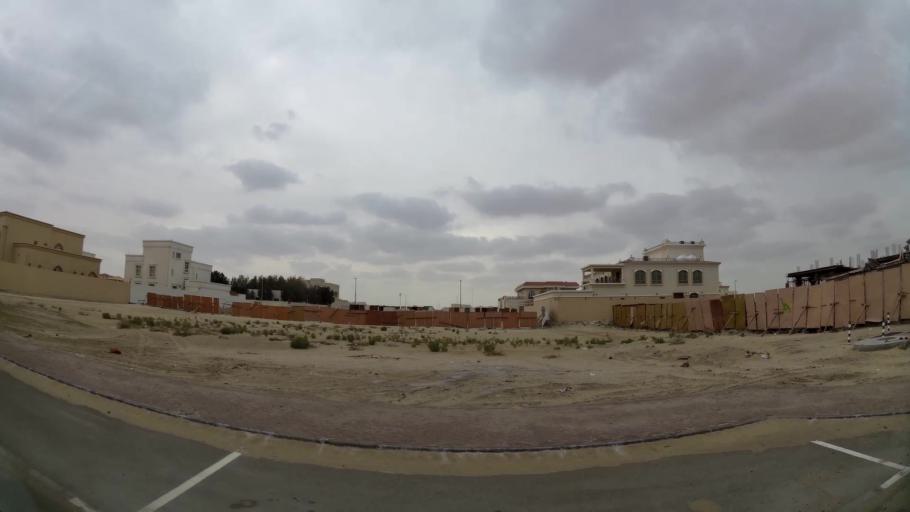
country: AE
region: Abu Dhabi
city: Abu Dhabi
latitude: 24.3713
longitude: 54.6289
